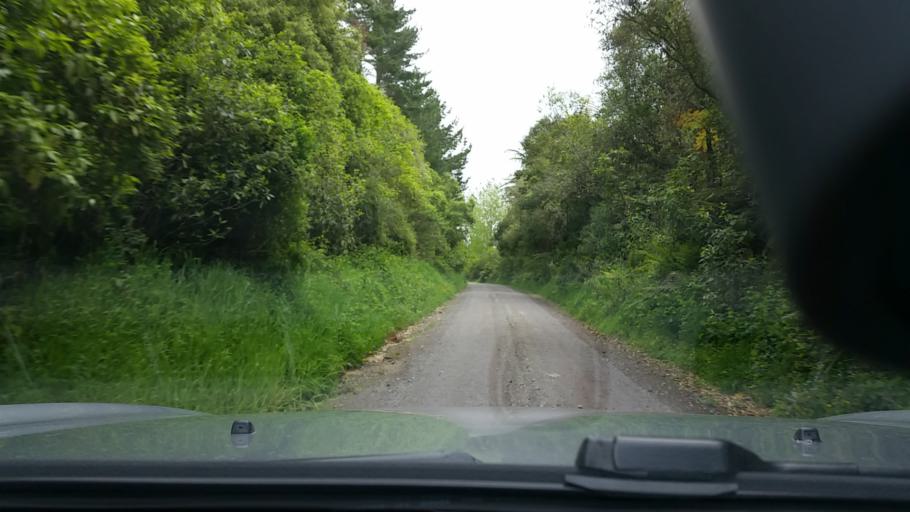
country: NZ
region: Bay of Plenty
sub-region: Rotorua District
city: Rotorua
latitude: -38.4038
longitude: 176.1413
